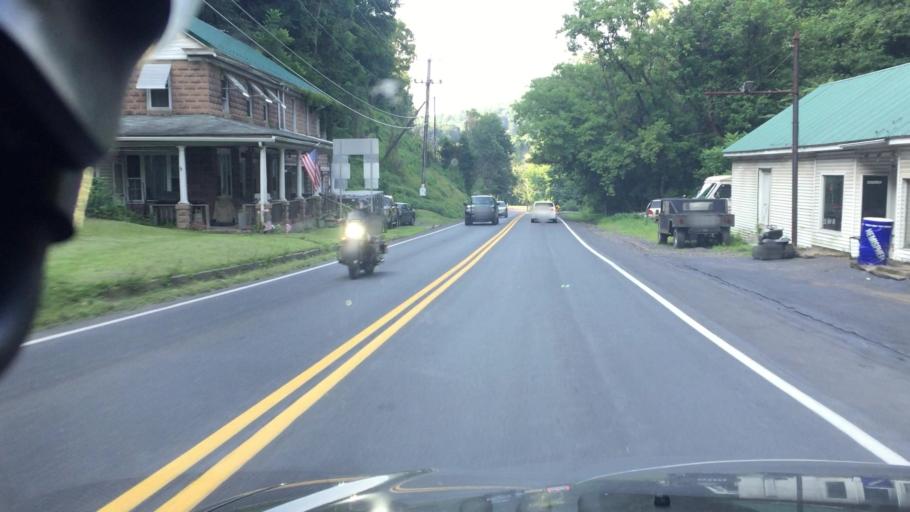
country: US
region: Pennsylvania
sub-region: Columbia County
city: Catawissa
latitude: 40.9435
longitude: -76.4569
